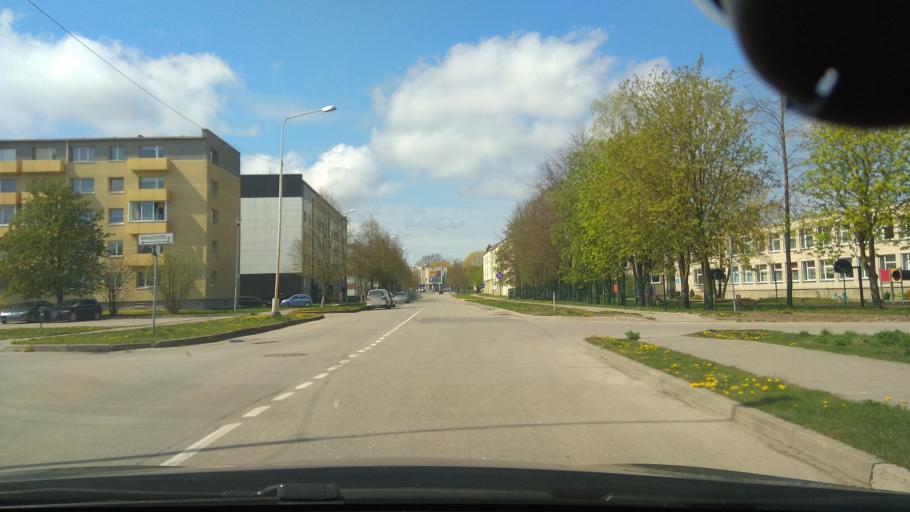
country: LT
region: Siauliu apskritis
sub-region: Joniskis
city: Joniskis
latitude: 56.2422
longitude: 23.6224
